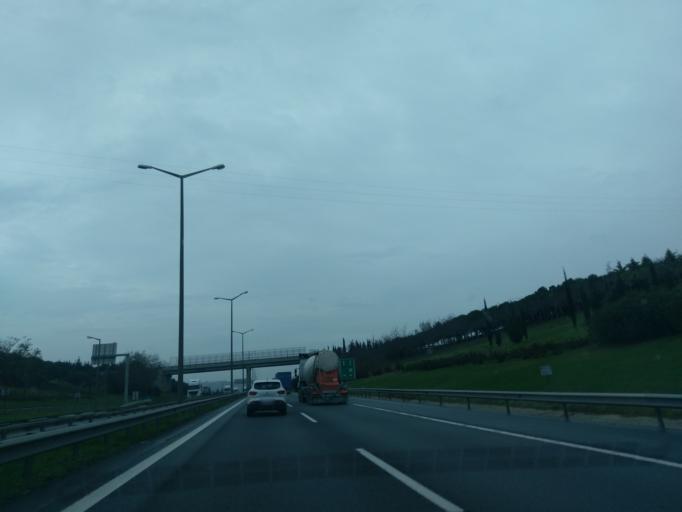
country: TR
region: Istanbul
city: Silivri
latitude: 41.1124
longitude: 28.2631
